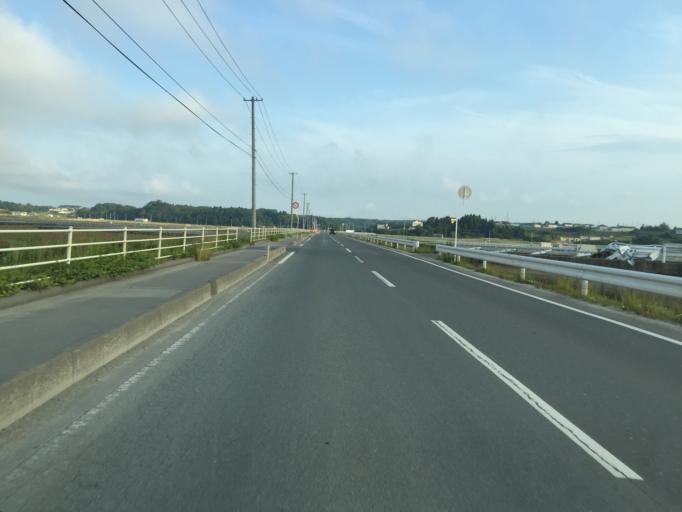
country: JP
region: Miyagi
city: Marumori
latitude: 37.7737
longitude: 140.9810
